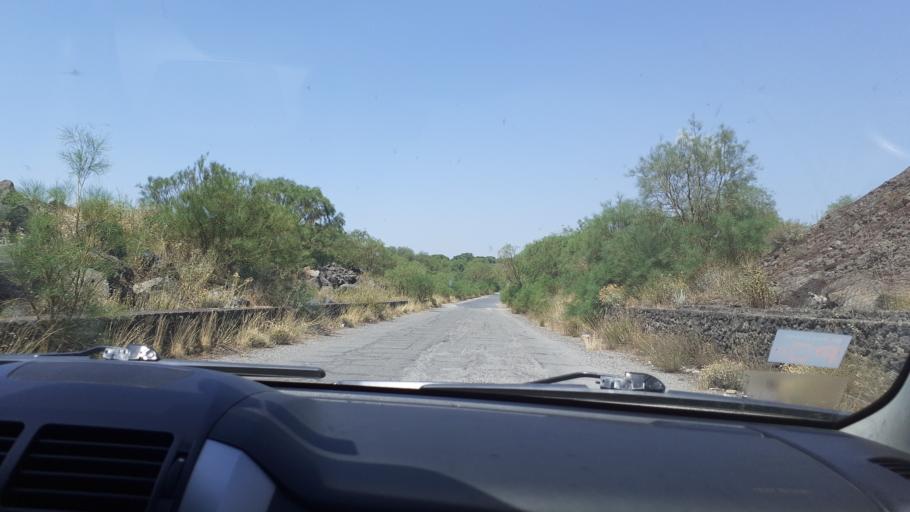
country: IT
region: Sicily
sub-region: Catania
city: Nicolosi
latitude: 37.6449
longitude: 14.9985
